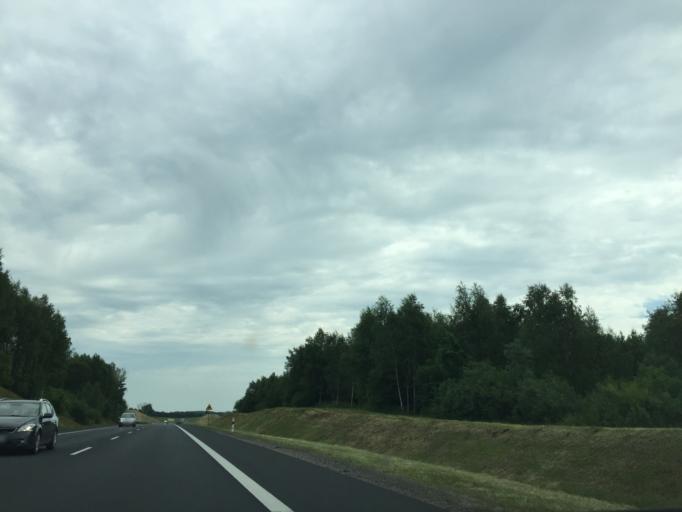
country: PL
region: Warmian-Masurian Voivodeship
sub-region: Powiat olsztynski
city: Biskupiec
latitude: 53.8312
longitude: 20.8986
